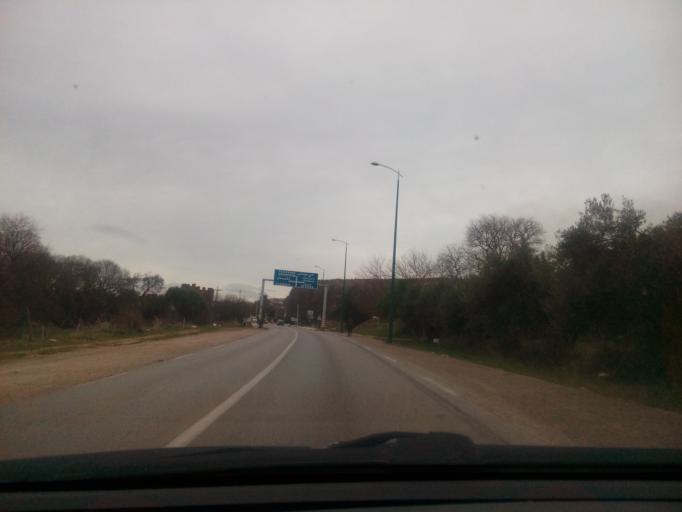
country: DZ
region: Tlemcen
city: Mansoura
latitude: 34.8642
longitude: -1.3356
